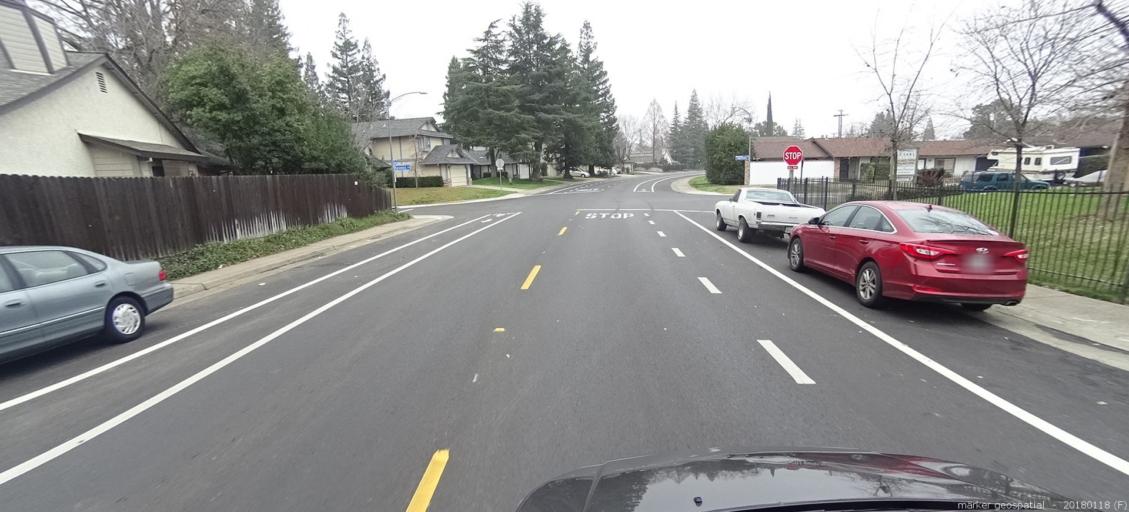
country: US
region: California
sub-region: Sacramento County
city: Rancho Cordova
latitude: 38.5856
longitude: -121.3204
